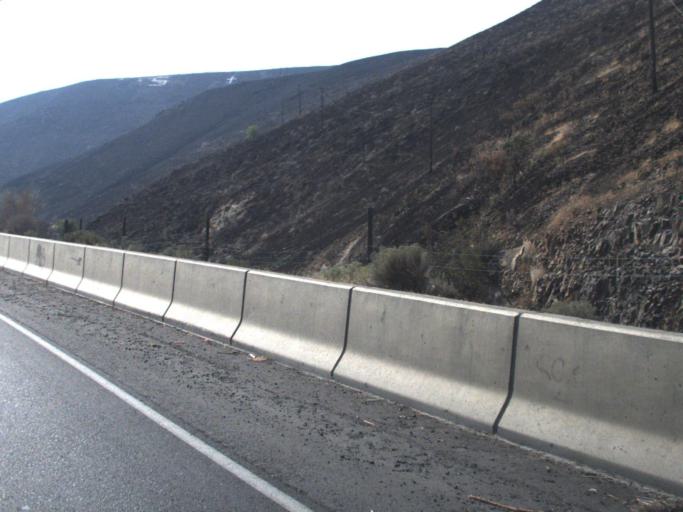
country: US
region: Washington
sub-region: Yakima County
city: Selah
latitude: 46.6407
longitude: -120.5300
